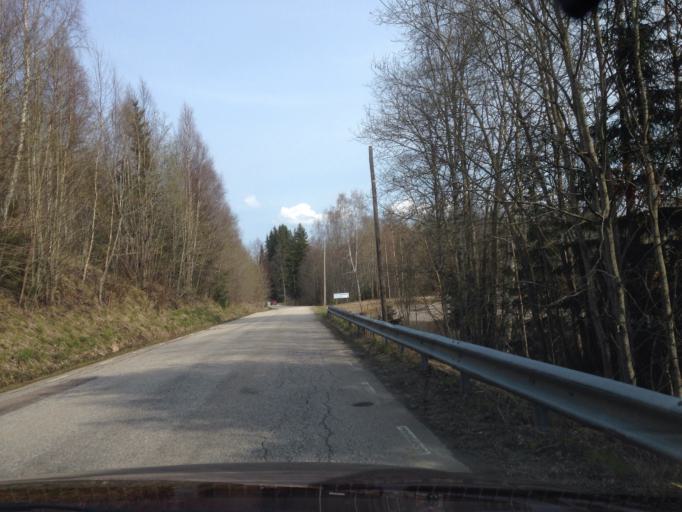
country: SE
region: Dalarna
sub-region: Ludvika Kommun
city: Grangesberg
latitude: 60.0859
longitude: 14.9935
